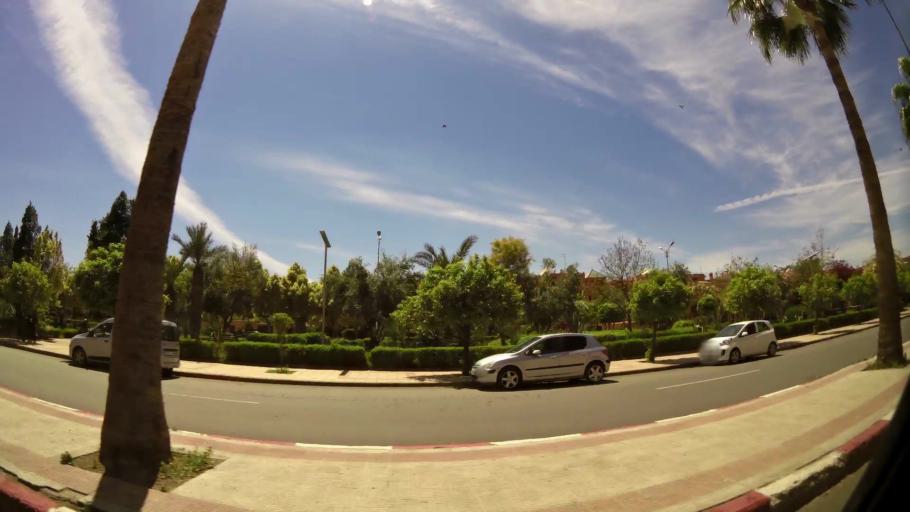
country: MA
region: Marrakech-Tensift-Al Haouz
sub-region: Marrakech
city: Marrakesh
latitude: 31.6626
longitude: -8.0081
